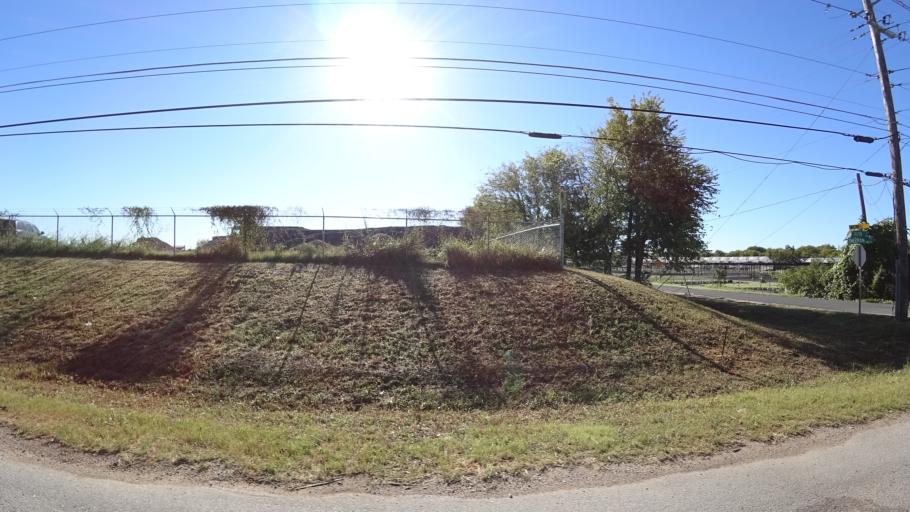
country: US
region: Texas
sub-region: Travis County
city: Austin
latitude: 30.2301
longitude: -97.6708
